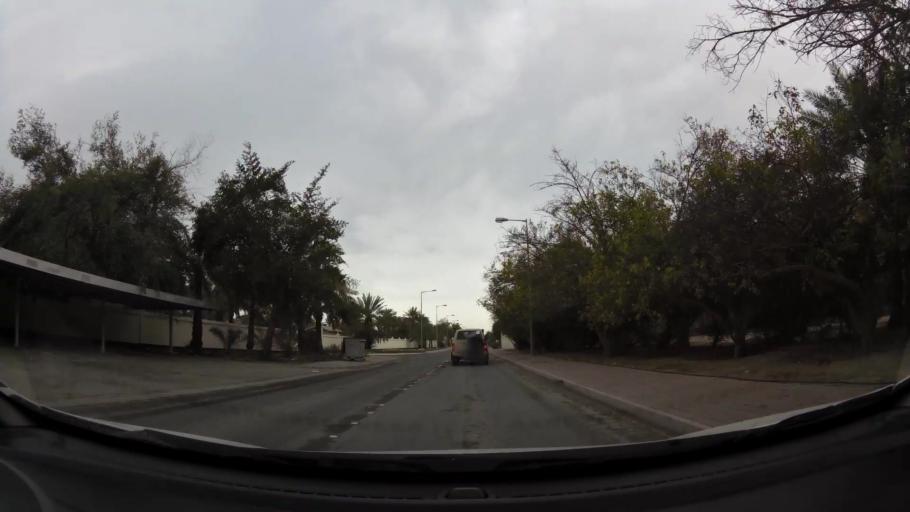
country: BH
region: Central Governorate
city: Madinat Hamad
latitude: 26.1592
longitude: 50.4517
